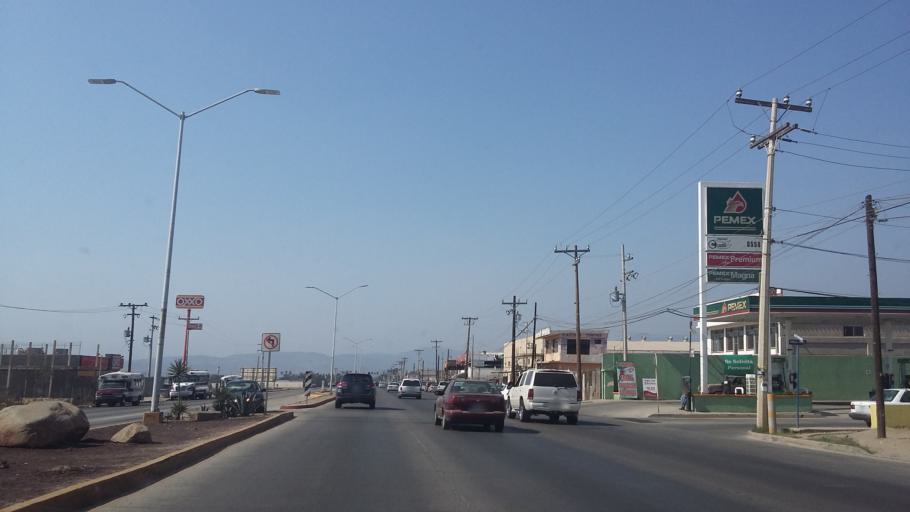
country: MX
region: Baja California
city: Rodolfo Sanchez Taboada
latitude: 31.7862
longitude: -116.5919
